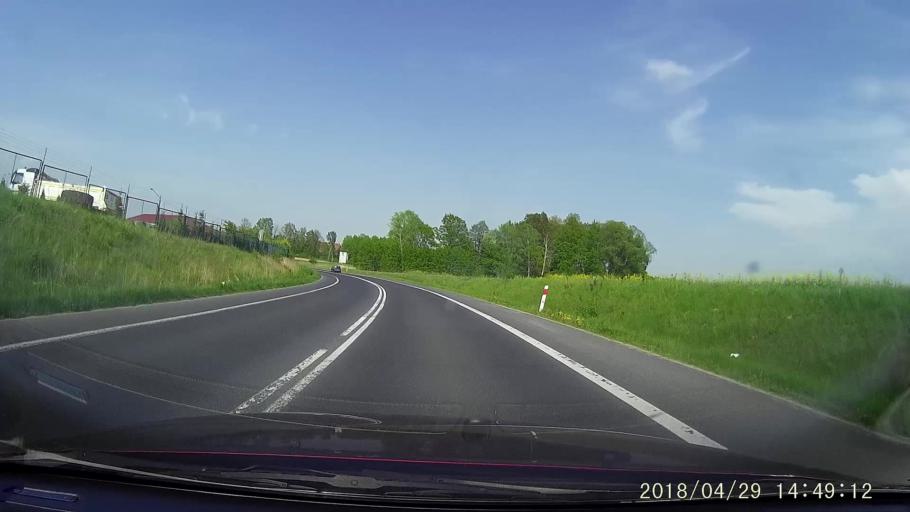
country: PL
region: Lower Silesian Voivodeship
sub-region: Powiat zgorzelecki
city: Zgorzelec
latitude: 51.1274
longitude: 15.0191
